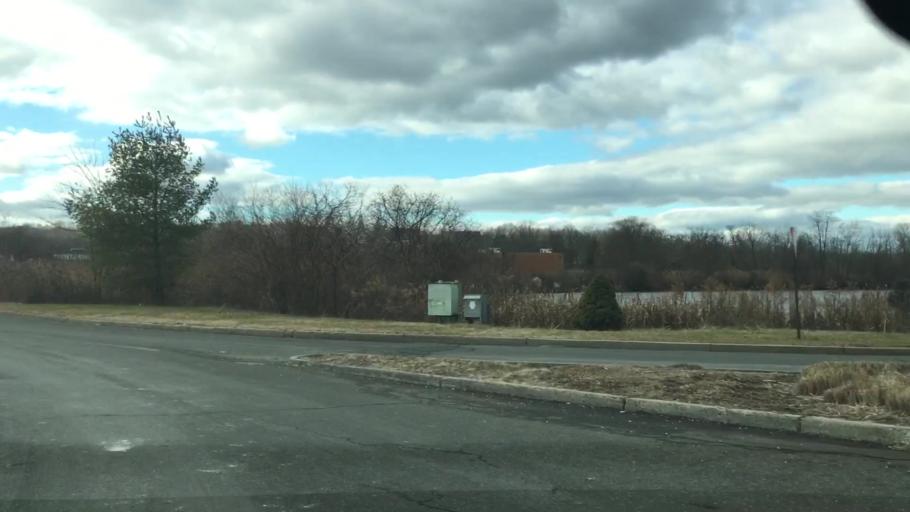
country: US
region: Connecticut
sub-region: Fairfield County
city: Danbury
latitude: 41.3776
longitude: -73.4843
